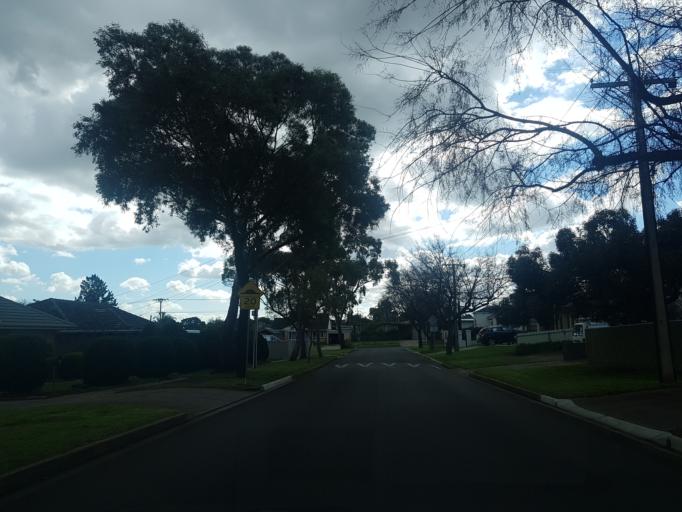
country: AU
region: South Australia
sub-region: Salisbury
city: Ingle Farm
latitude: -34.8130
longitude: 138.6495
